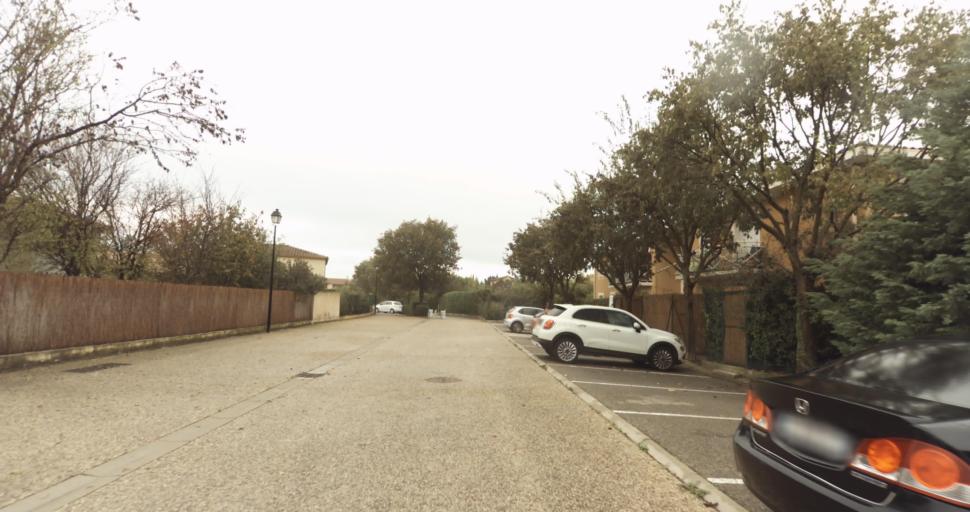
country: FR
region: Provence-Alpes-Cote d'Azur
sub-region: Departement des Bouches-du-Rhone
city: Rognonas
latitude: 43.9029
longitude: 4.8117
